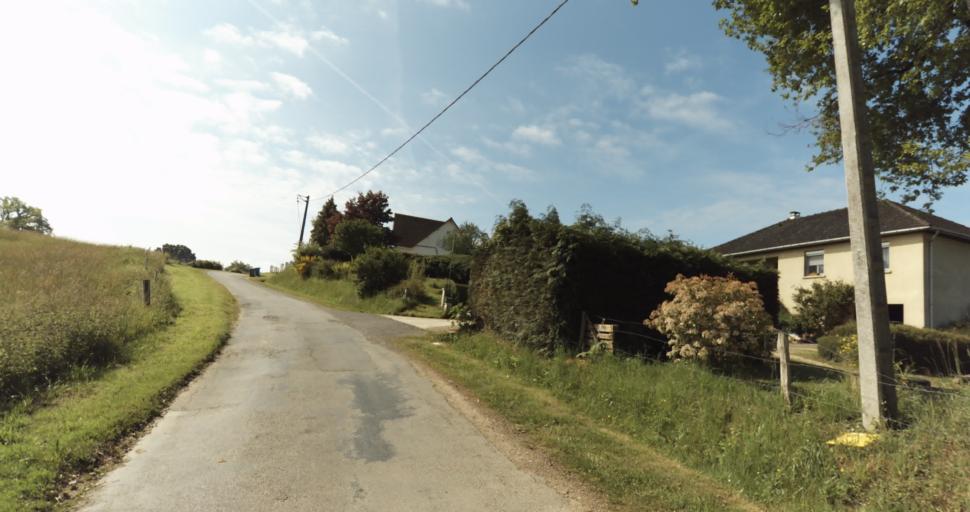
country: FR
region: Limousin
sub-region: Departement de la Haute-Vienne
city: Solignac
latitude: 45.7067
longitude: 1.2600
